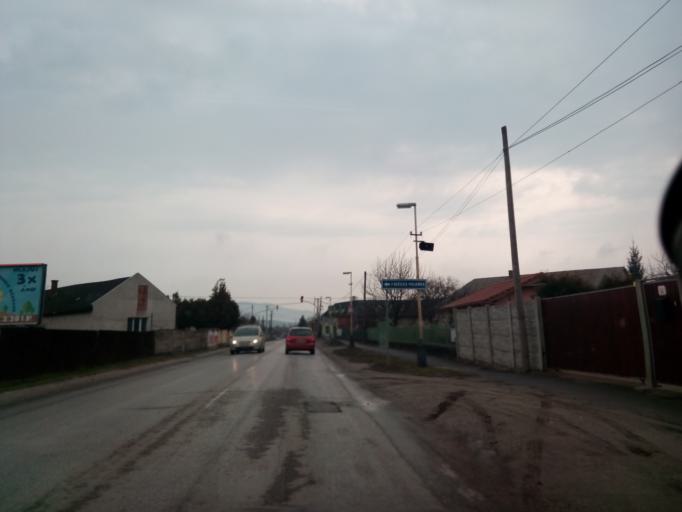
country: SK
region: Kosicky
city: Kosice
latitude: 48.6687
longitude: 21.3188
